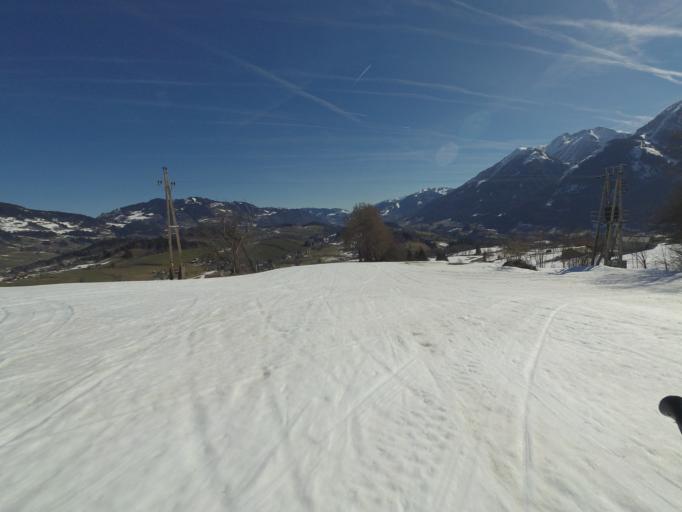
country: AT
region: Salzburg
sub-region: Politischer Bezirk Zell am See
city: Lend
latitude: 47.3105
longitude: 13.0746
